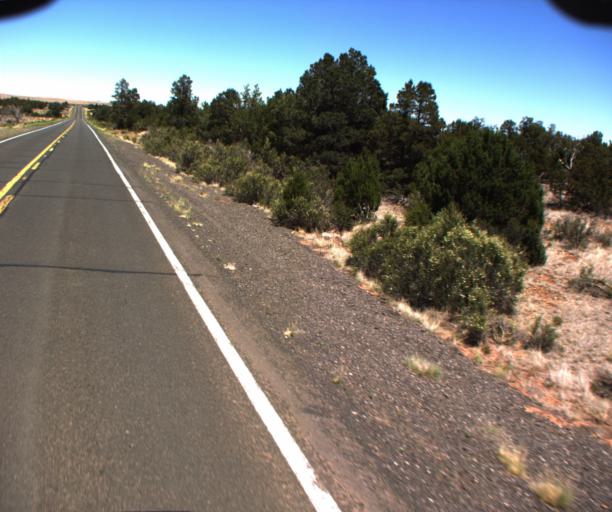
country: US
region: Arizona
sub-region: Coconino County
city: LeChee
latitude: 34.7131
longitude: -111.0931
